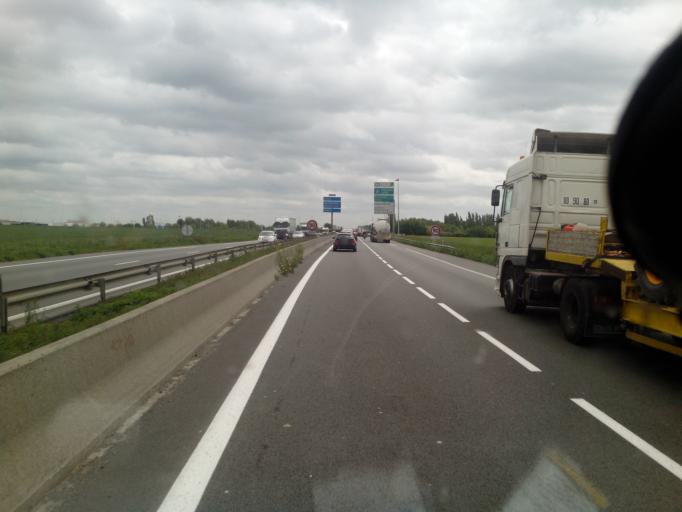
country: FR
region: Nord-Pas-de-Calais
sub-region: Departement du Nord
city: Ennetieres-en-Weppes
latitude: 50.6323
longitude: 2.9532
